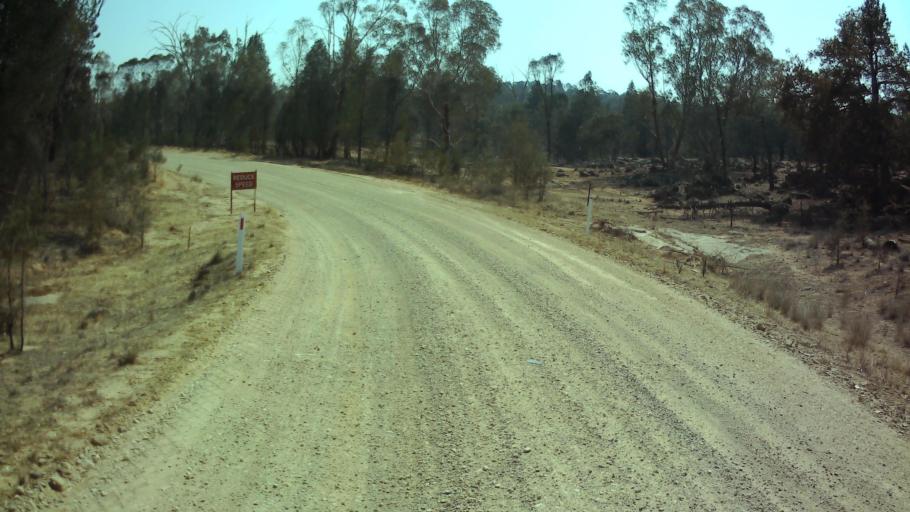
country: AU
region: New South Wales
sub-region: Weddin
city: Grenfell
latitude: -33.6618
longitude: 148.2749
